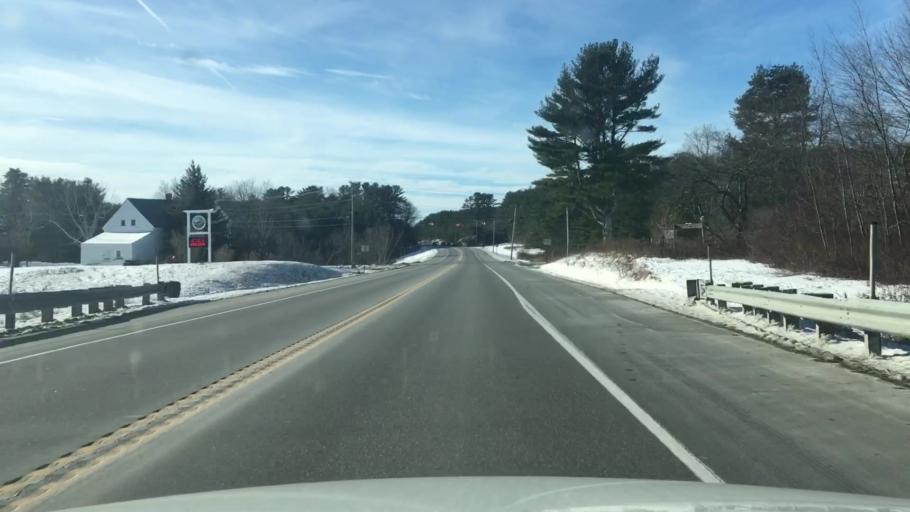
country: US
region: Maine
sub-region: Sagadahoc County
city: Woolwich
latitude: 43.9350
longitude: -69.7773
